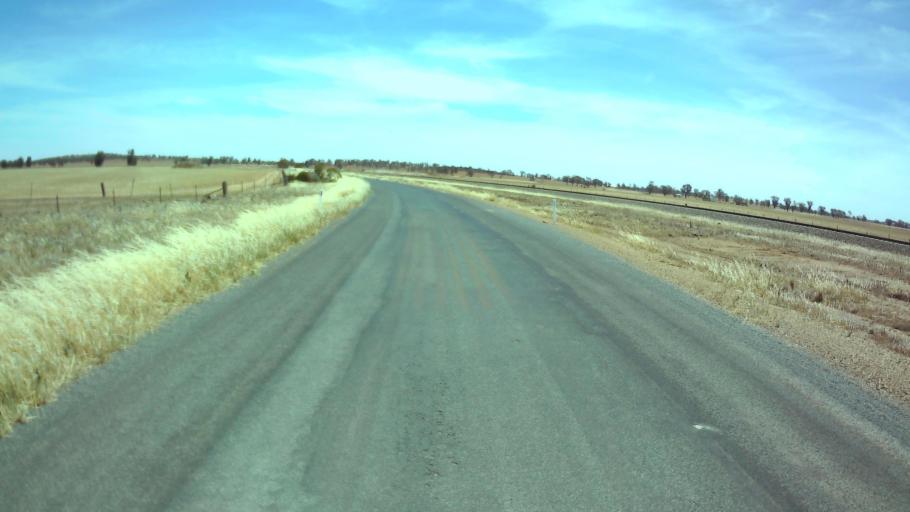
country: AU
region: New South Wales
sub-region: Weddin
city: Grenfell
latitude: -33.7550
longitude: 147.7635
